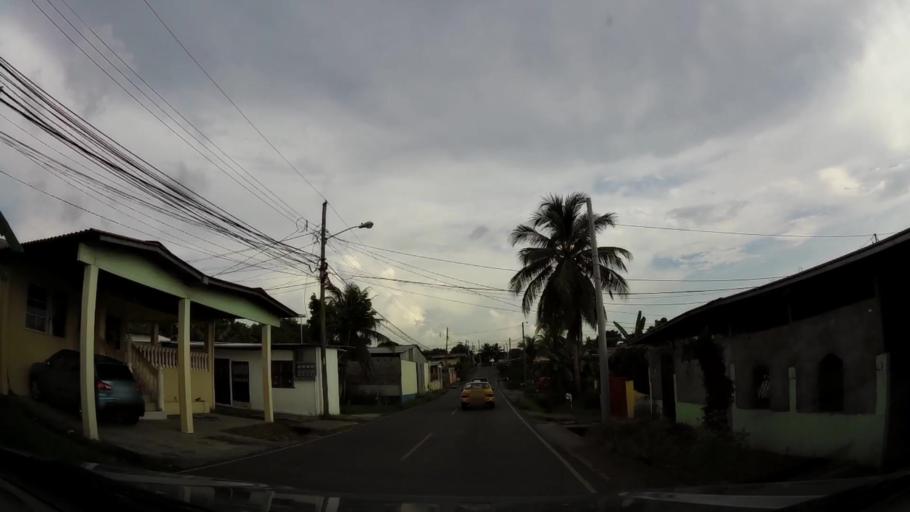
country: PA
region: Panama
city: Tocumen
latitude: 9.1054
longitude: -79.3646
